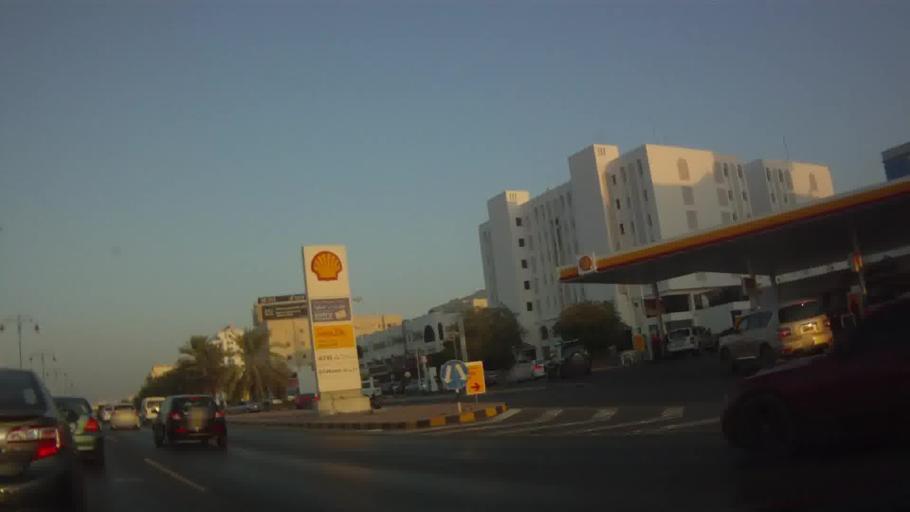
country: OM
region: Muhafazat Masqat
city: Bawshar
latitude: 23.5971
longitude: 58.4189
